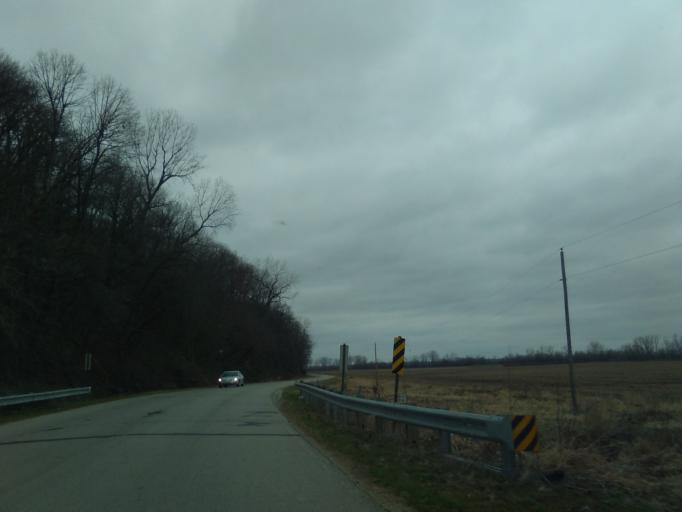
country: US
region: Missouri
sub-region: Holt County
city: Mound City
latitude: 40.0246
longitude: -95.3590
